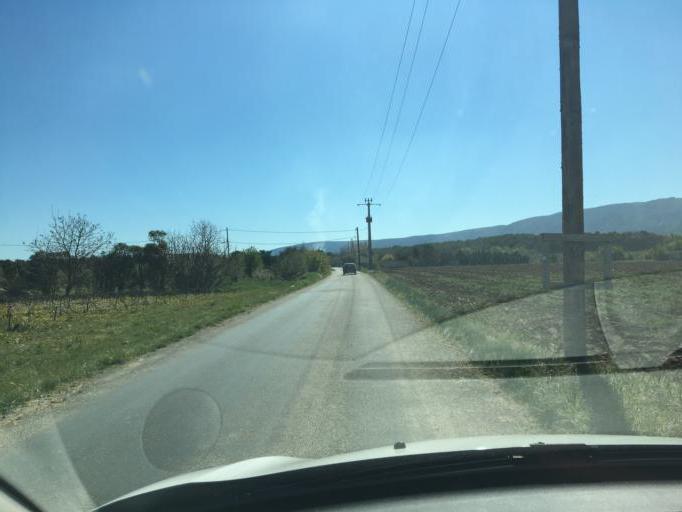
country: FR
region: Provence-Alpes-Cote d'Azur
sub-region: Departement du Vaucluse
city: Maubec
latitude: 43.8625
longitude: 5.1283
